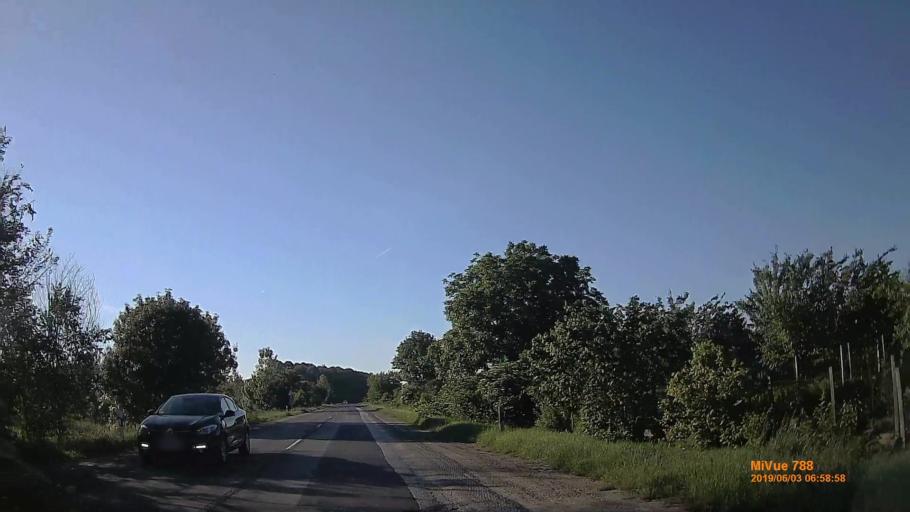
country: HU
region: Pest
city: Dabas
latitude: 47.2158
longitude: 19.2776
